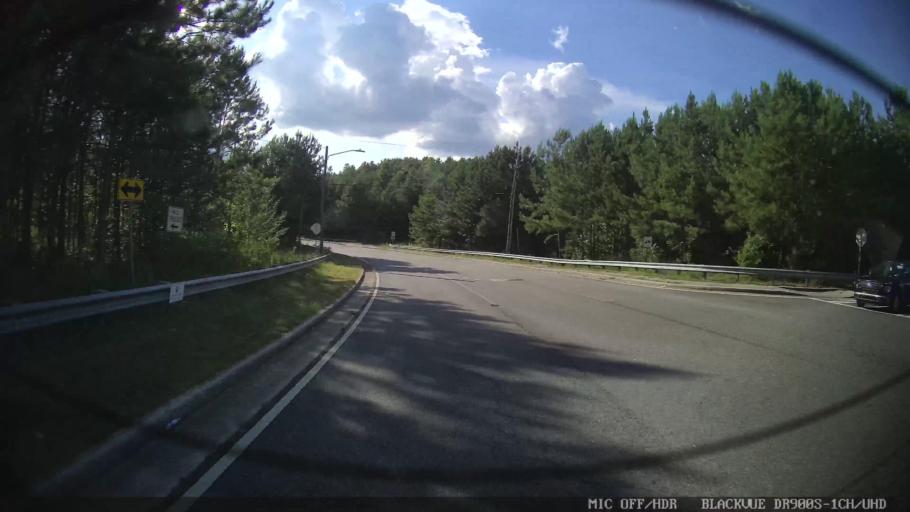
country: US
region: Georgia
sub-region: Floyd County
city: Rome
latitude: 34.2208
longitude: -85.1331
